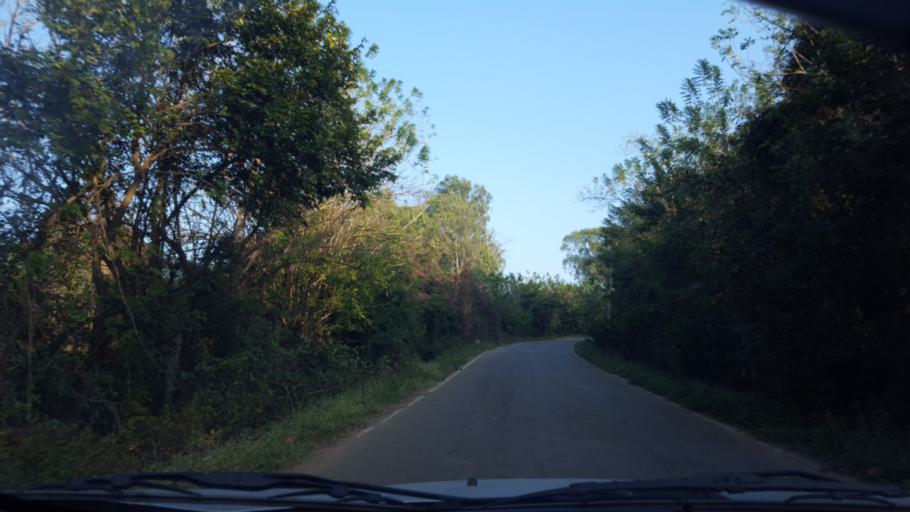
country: IN
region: Karnataka
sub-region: Bangalore Urban
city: Yelahanka
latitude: 13.1753
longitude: 77.5932
